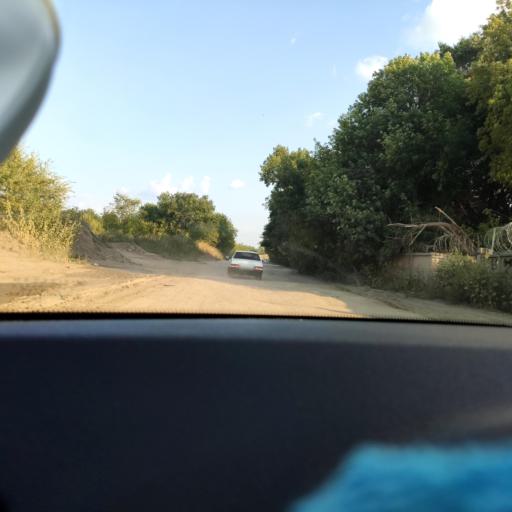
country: RU
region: Samara
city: Samara
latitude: 53.1821
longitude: 50.2637
